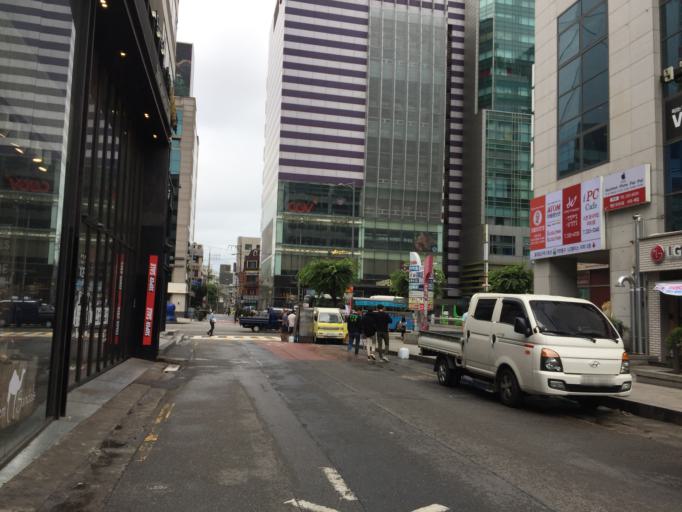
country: KR
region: Seoul
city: Seoul
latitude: 37.5557
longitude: 126.9232
